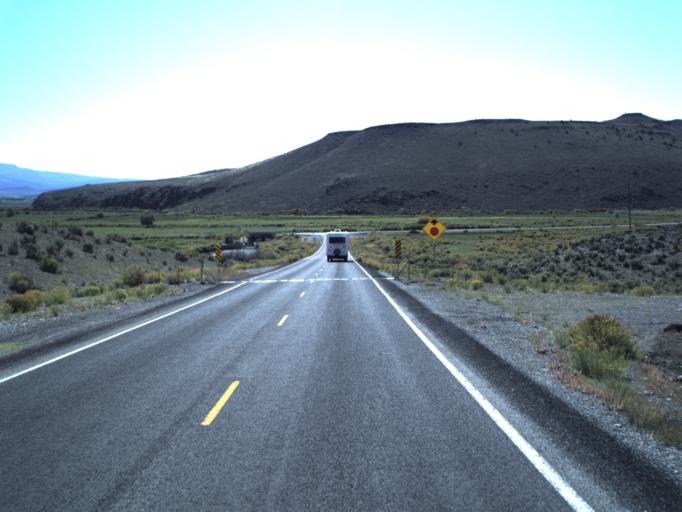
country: US
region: Utah
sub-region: Piute County
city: Junction
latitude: 38.1695
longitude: -112.0271
